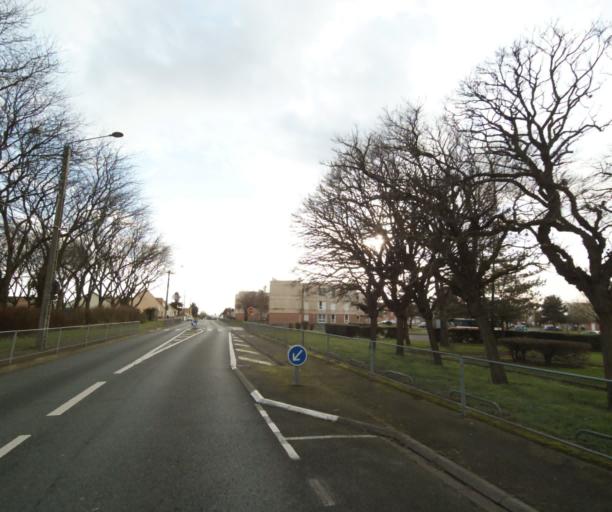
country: FR
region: Pays de la Loire
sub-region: Departement de la Sarthe
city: Le Mans
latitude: 47.9640
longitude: 0.2092
